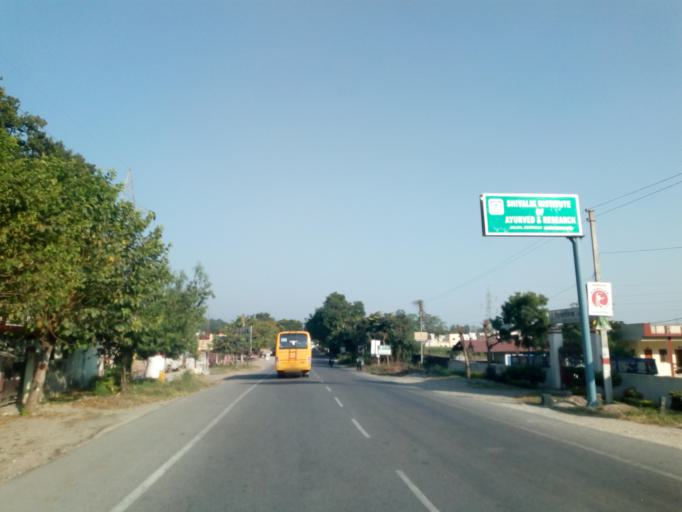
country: IN
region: Uttarakhand
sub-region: Dehradun
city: Dehradun
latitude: 30.3460
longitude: 77.8984
